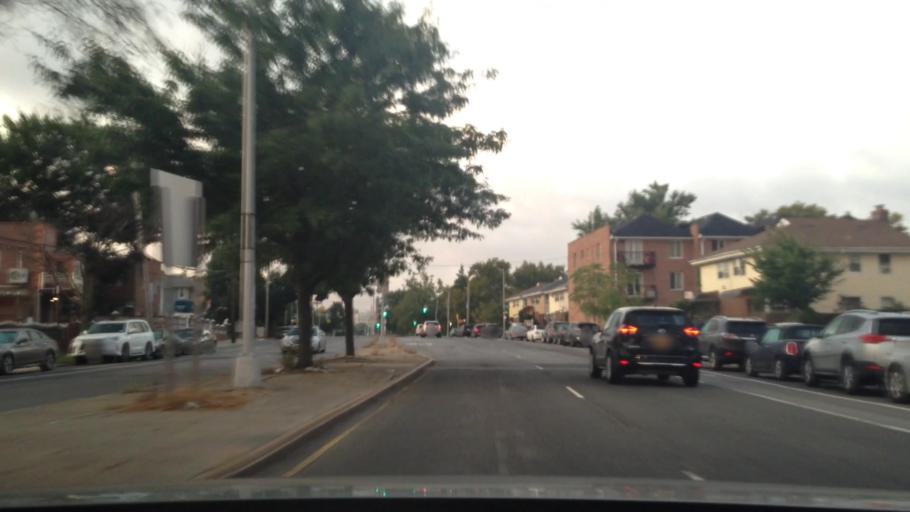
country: US
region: New York
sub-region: Queens County
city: Jamaica
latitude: 40.7294
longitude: -73.8053
